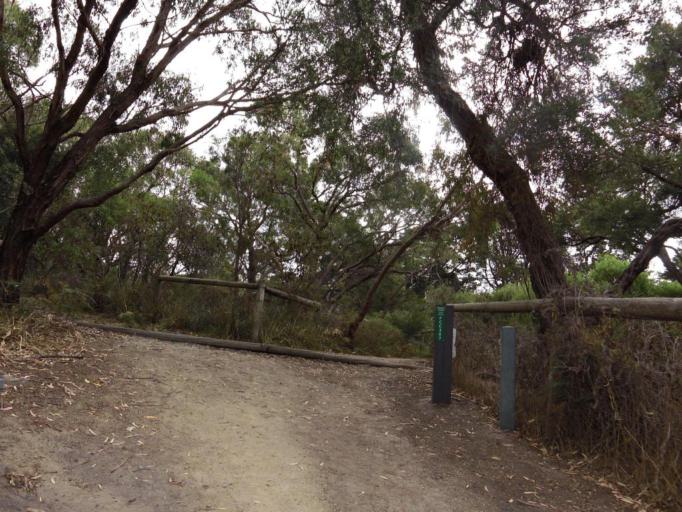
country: AU
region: Victoria
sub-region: Frankston
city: Frankston
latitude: -38.1609
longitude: 145.1105
